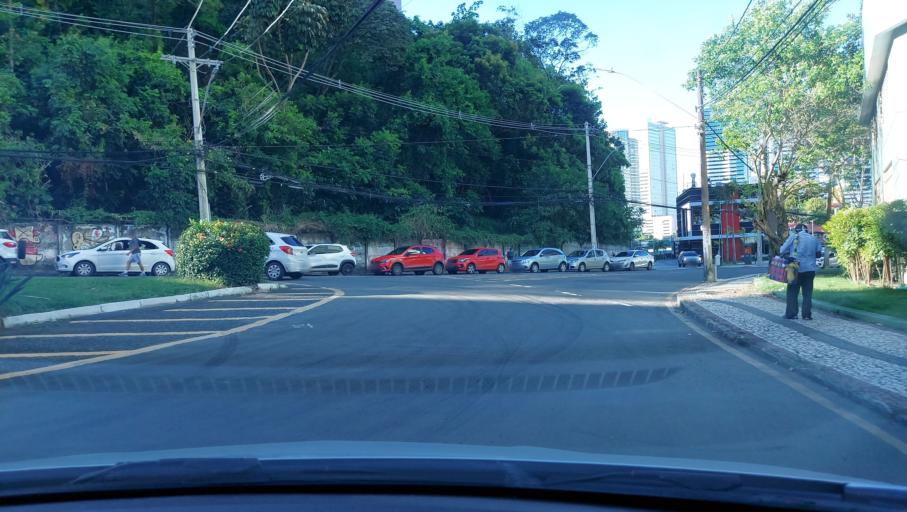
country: BR
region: Bahia
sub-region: Salvador
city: Salvador
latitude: -12.9857
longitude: -38.4529
